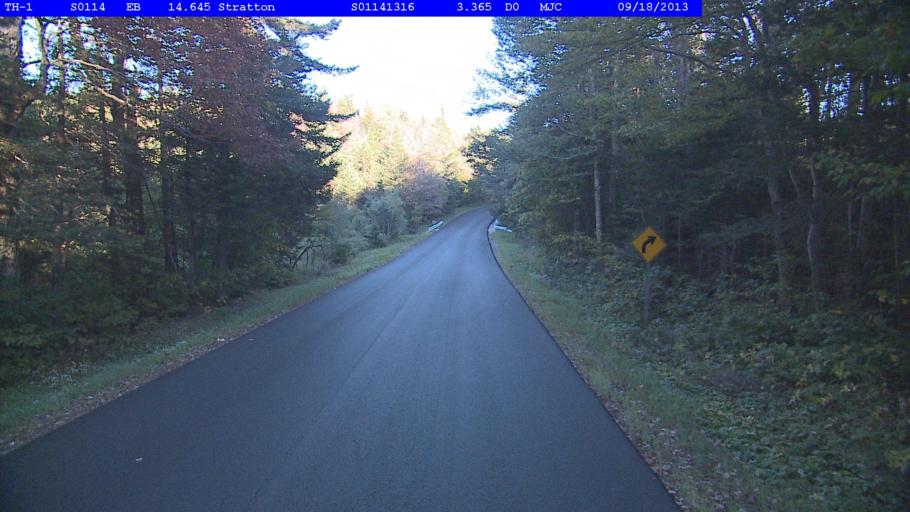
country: US
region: Vermont
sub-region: Bennington County
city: Manchester Center
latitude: 43.0576
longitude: -72.9403
